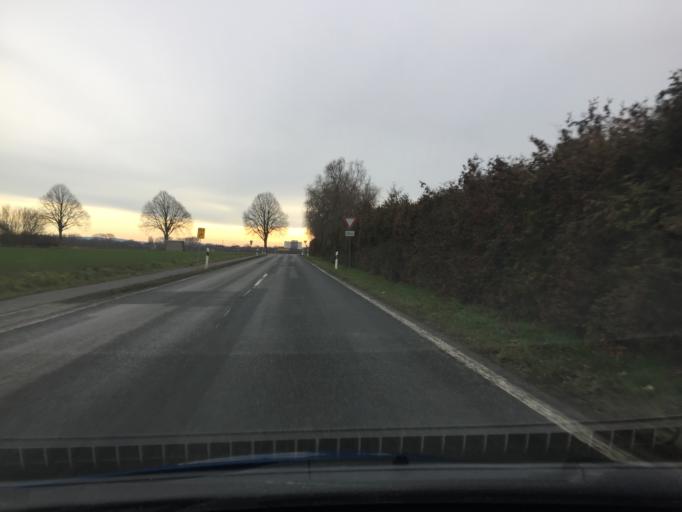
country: DE
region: Lower Saxony
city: Pattensen
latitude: 52.2807
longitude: 9.7661
